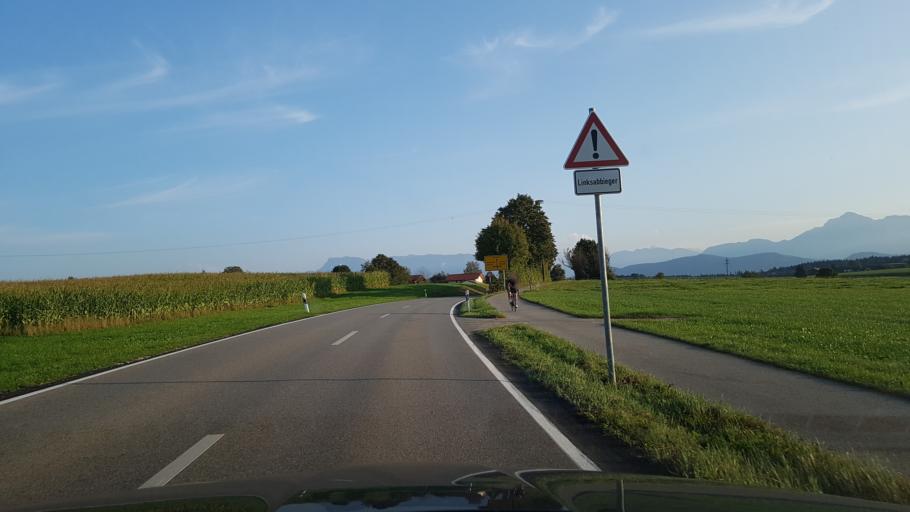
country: DE
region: Bavaria
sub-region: Upper Bavaria
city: Laufen
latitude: 47.8916
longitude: 12.9229
